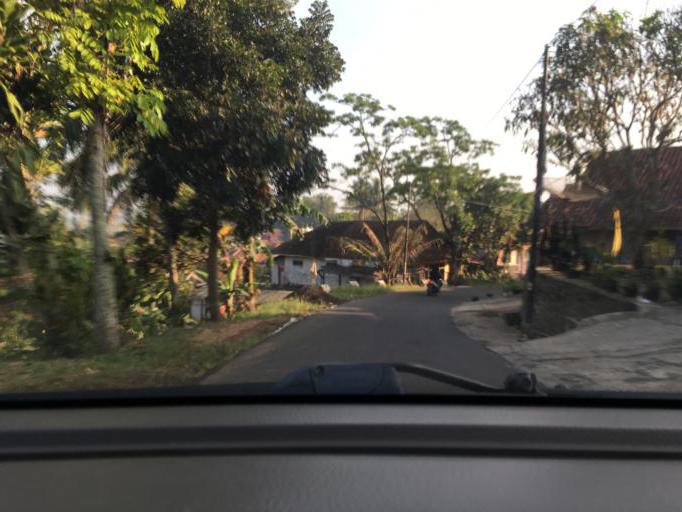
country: ID
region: West Java
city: Maniis
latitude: -7.0402
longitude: 108.3138
